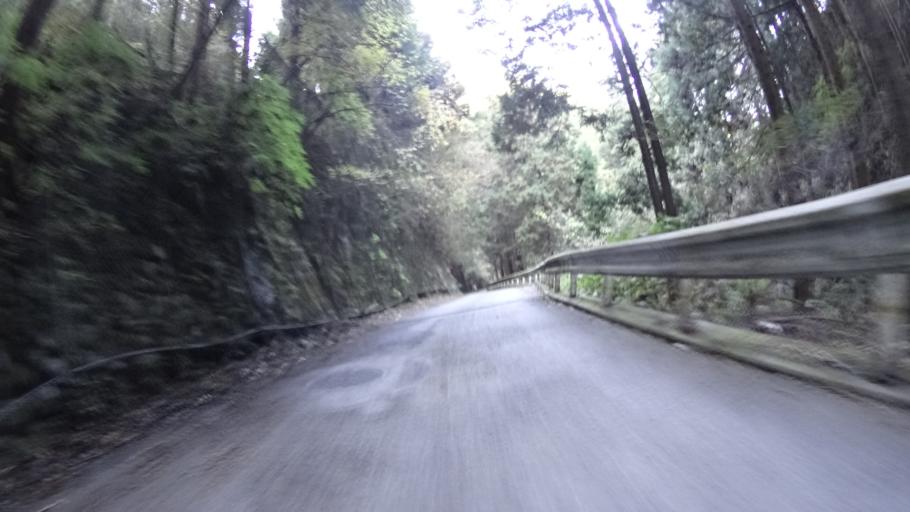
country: JP
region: Yamanashi
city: Uenohara
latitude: 35.6584
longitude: 139.1721
